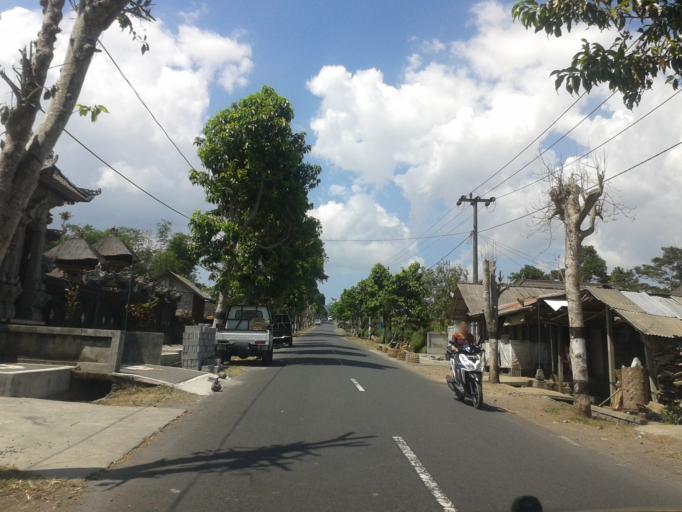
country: ID
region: Bali
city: Banjar Tiga
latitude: -8.3237
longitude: 115.3280
